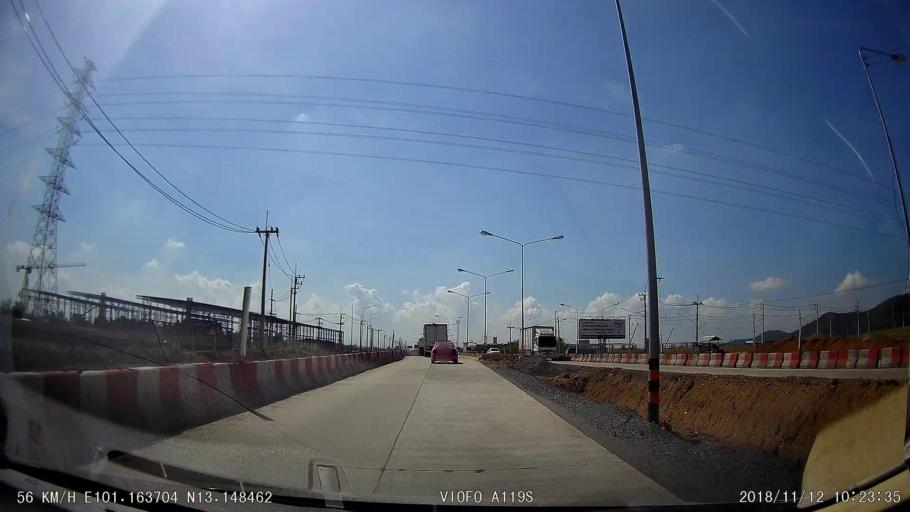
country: TH
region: Chon Buri
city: Ban Bueng
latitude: 13.1482
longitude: 101.1637
